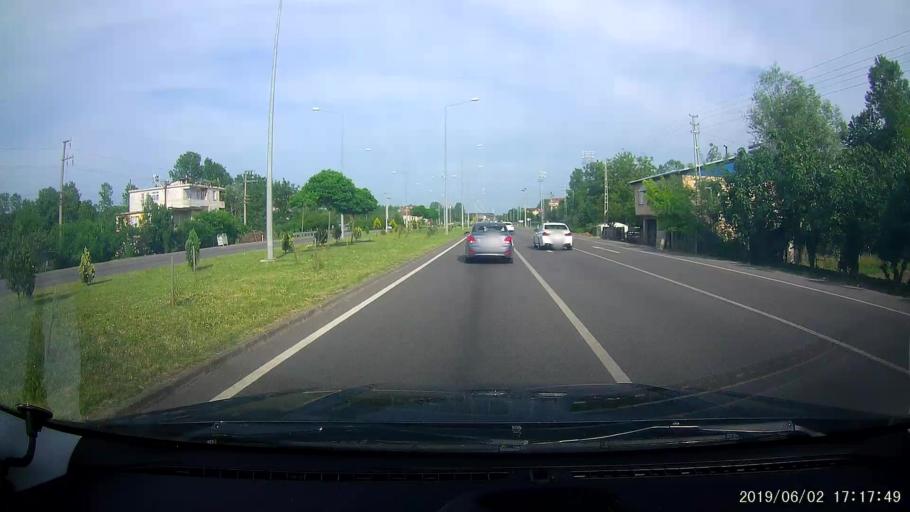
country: TR
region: Samsun
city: Dikbiyik
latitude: 41.2268
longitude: 36.5877
